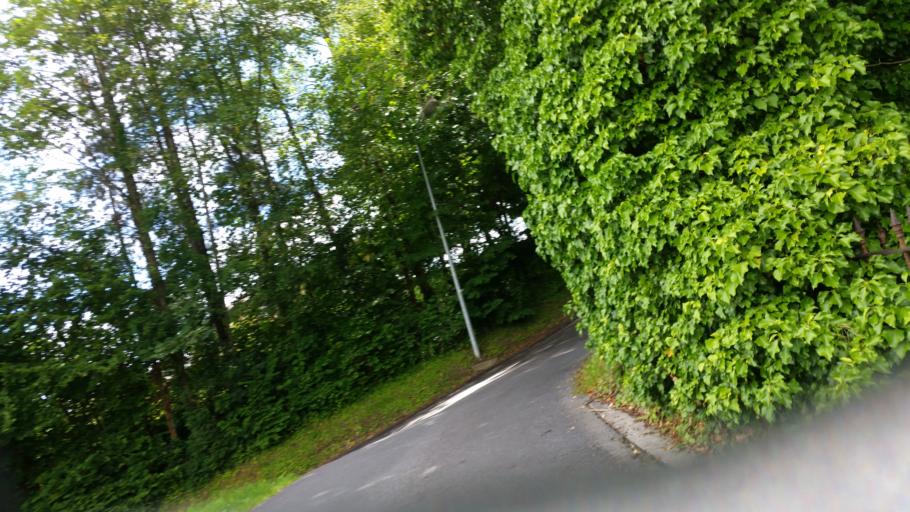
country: CH
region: Vaud
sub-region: Jura-Nord vaudois District
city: Yverdon-les-Bains
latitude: 46.7736
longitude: 6.6641
